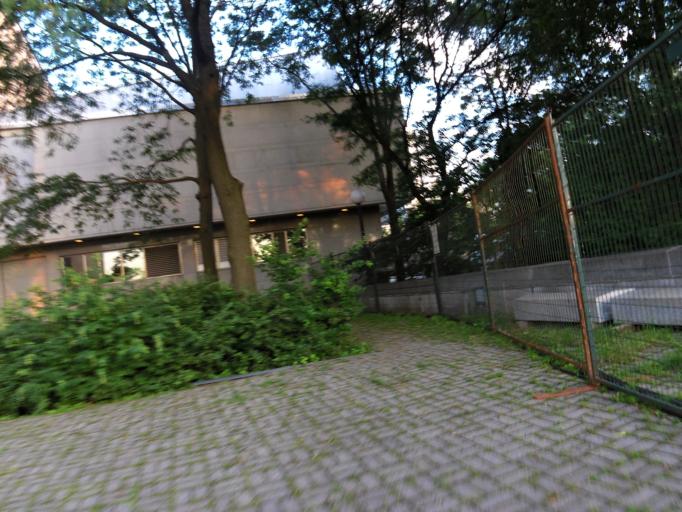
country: CA
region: Ontario
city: Ottawa
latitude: 45.4198
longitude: -75.7089
